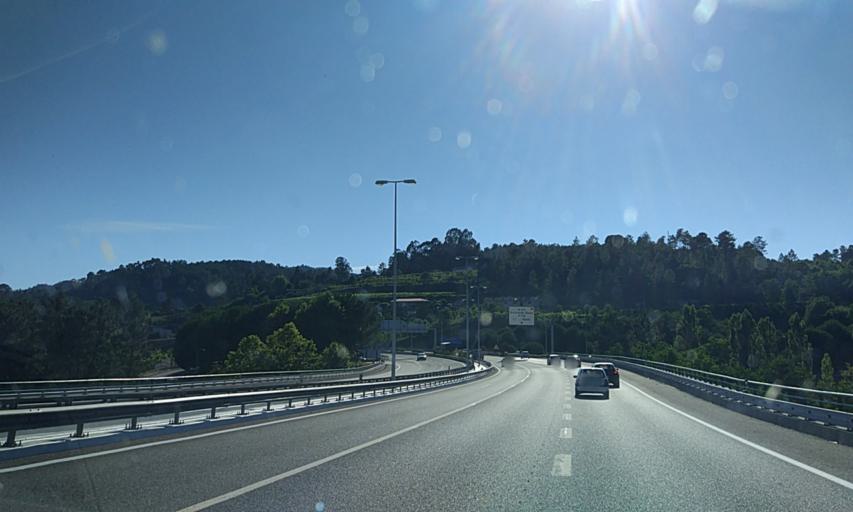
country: PT
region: Porto
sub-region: Amarante
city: Amarante
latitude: 41.2598
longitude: -8.0931
